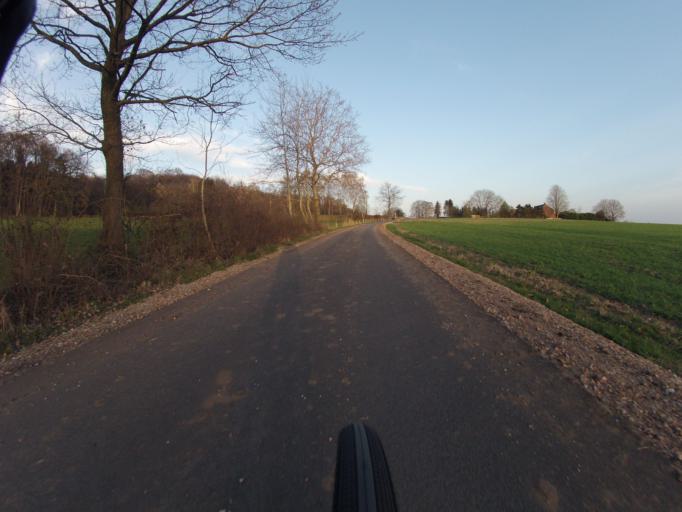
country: DE
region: North Rhine-Westphalia
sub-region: Regierungsbezirk Munster
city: Birgte
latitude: 52.2477
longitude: 7.6839
